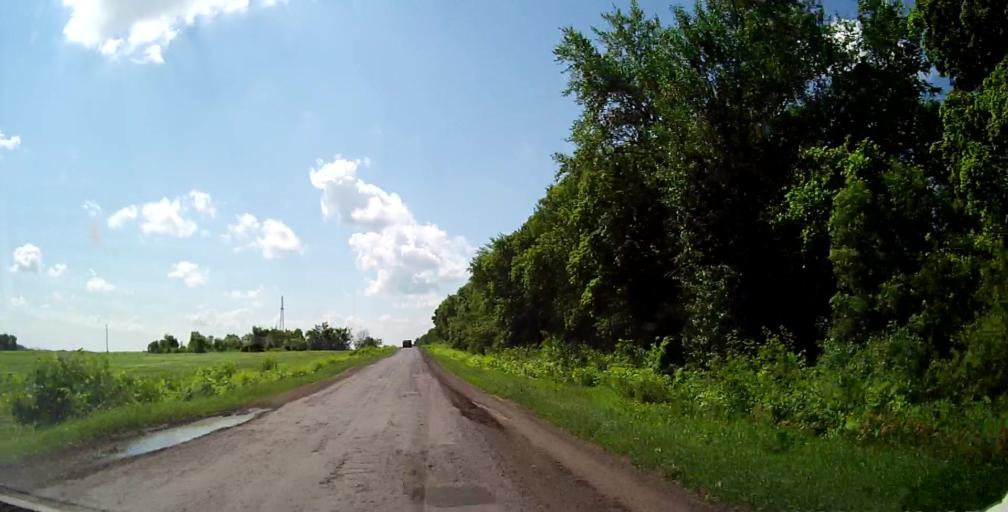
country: RU
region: Lipetsk
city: Chaplygin
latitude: 53.2949
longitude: 39.9559
